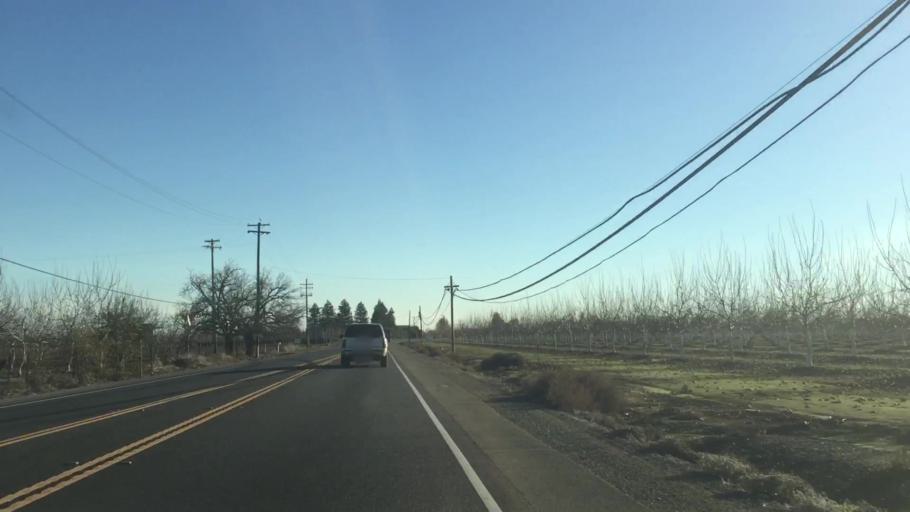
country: US
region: California
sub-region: Yuba County
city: Marysville
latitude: 39.2077
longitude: -121.5962
